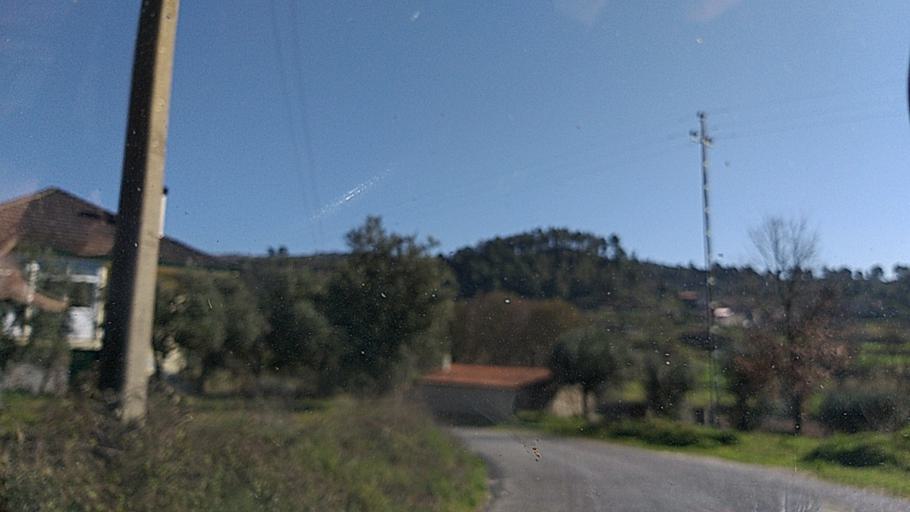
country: PT
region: Guarda
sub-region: Celorico da Beira
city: Celorico da Beira
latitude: 40.6863
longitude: -7.4034
